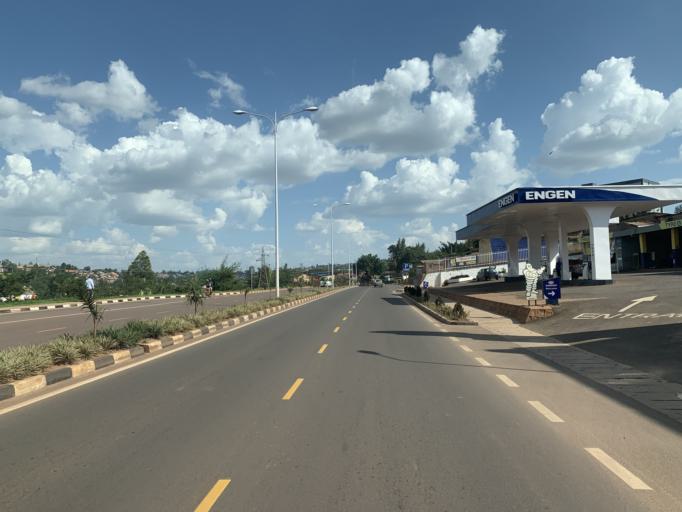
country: RW
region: Kigali
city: Kigali
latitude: -1.9674
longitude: 30.0826
